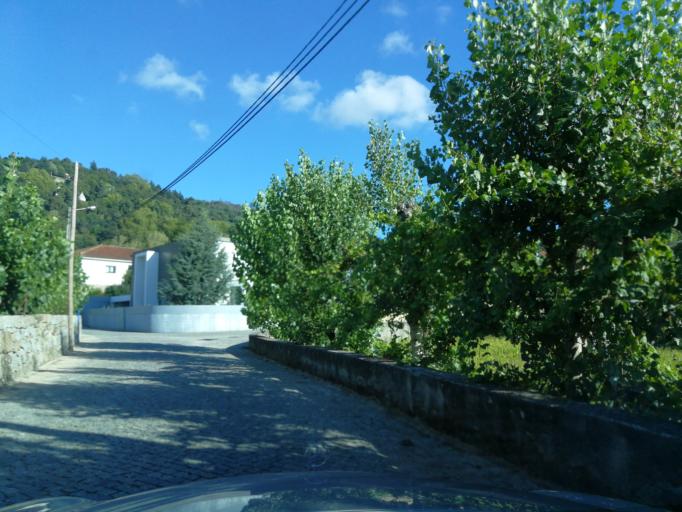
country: PT
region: Braga
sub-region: Braga
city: Adaufe
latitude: 41.5573
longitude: -8.3855
